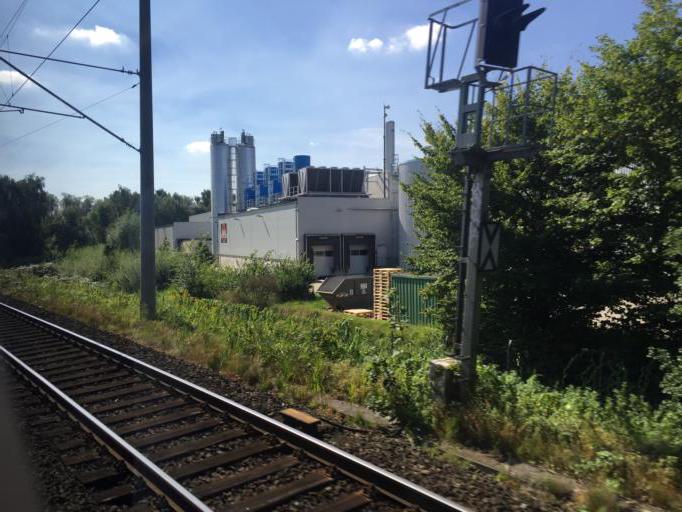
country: DE
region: Schleswig-Holstein
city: Bad Schwartau
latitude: 53.9037
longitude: 10.6921
